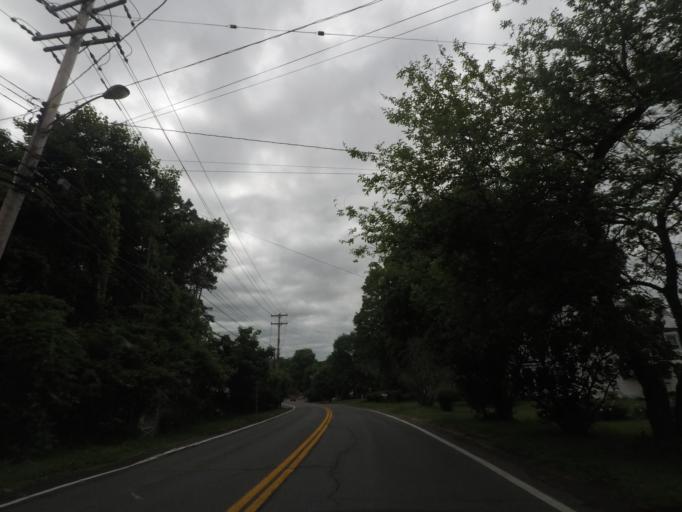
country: US
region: New York
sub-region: Columbia County
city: Philmont
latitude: 42.2521
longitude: -73.6605
